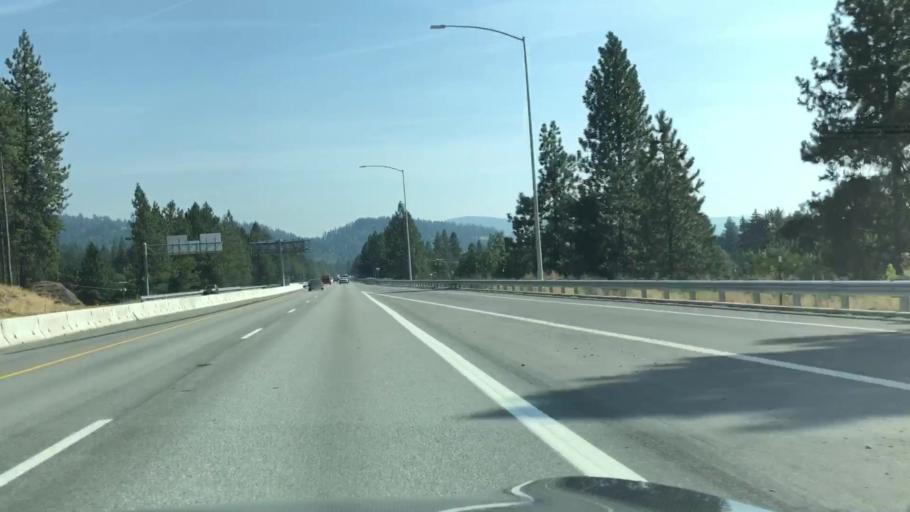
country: US
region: Idaho
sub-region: Kootenai County
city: Coeur d'Alene
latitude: 47.6848
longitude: -116.7612
